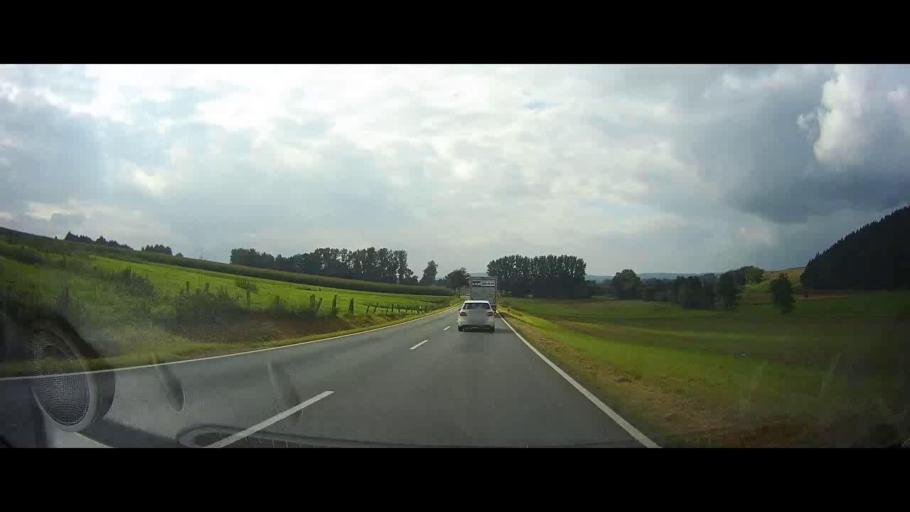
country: DE
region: Lower Saxony
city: Uslar
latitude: 51.6536
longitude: 9.6928
